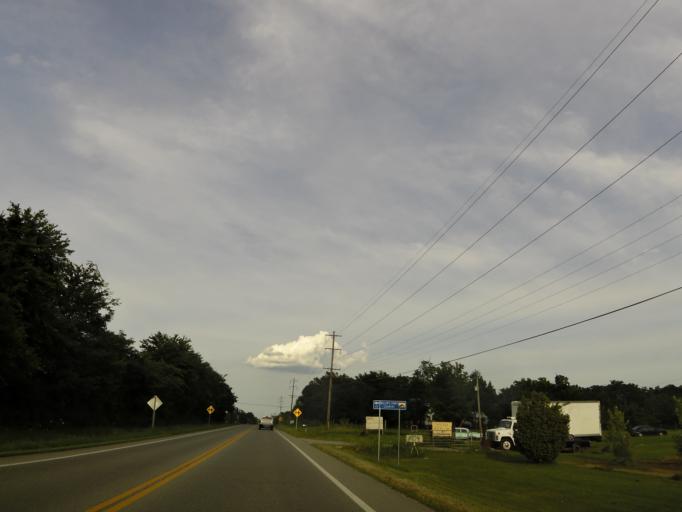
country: US
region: Tennessee
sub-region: Humphreys County
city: McEwen
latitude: 36.0915
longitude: -87.5223
